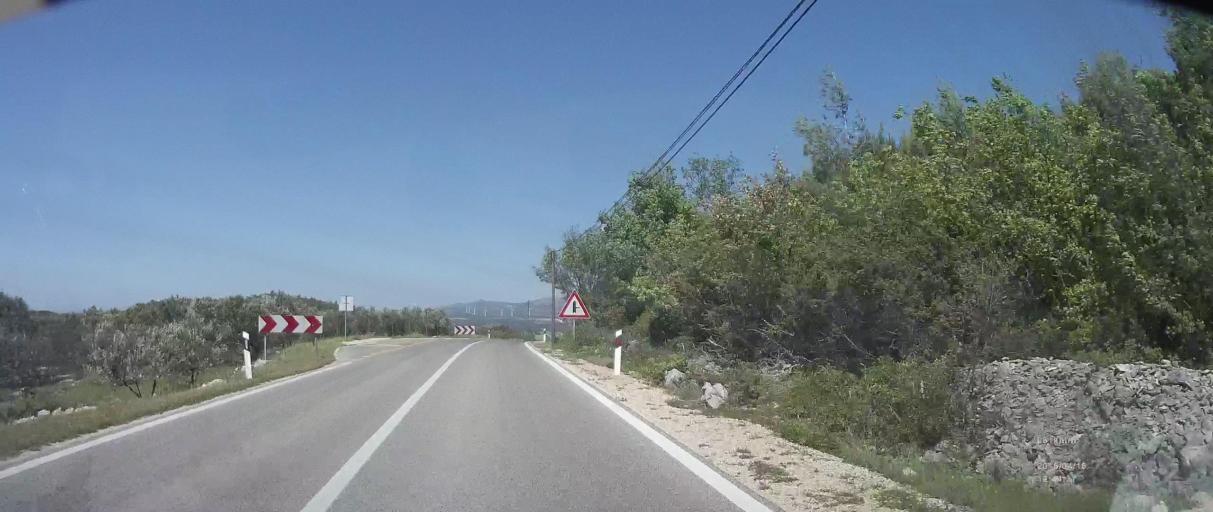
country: HR
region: Sibensko-Kniniska
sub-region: Grad Sibenik
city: Brodarica
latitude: 43.6432
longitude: 16.0633
